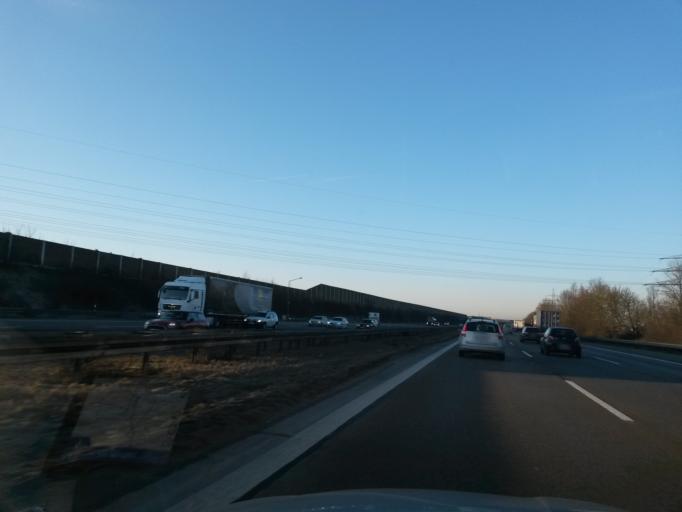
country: DE
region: Bavaria
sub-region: Upper Bavaria
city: Grasbrunn
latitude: 48.0861
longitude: 11.7413
